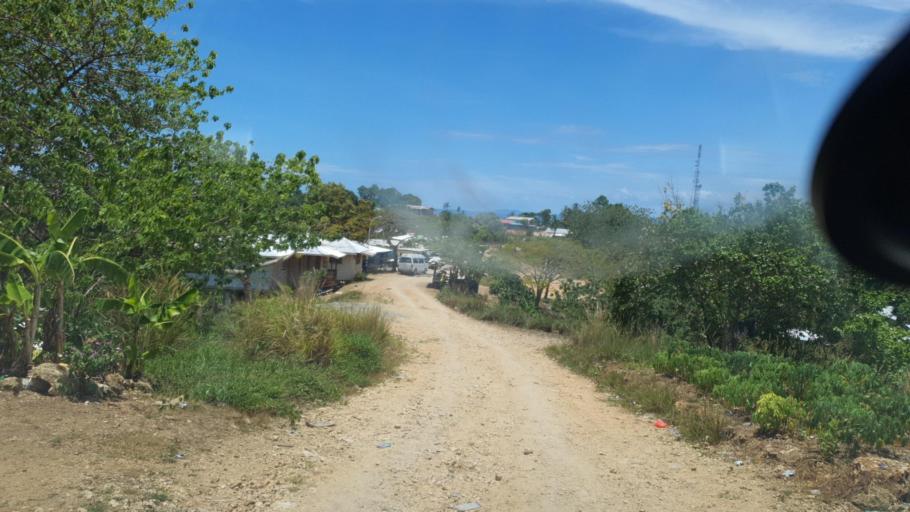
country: SB
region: Guadalcanal
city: Honiara
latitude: -9.4443
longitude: 159.9479
